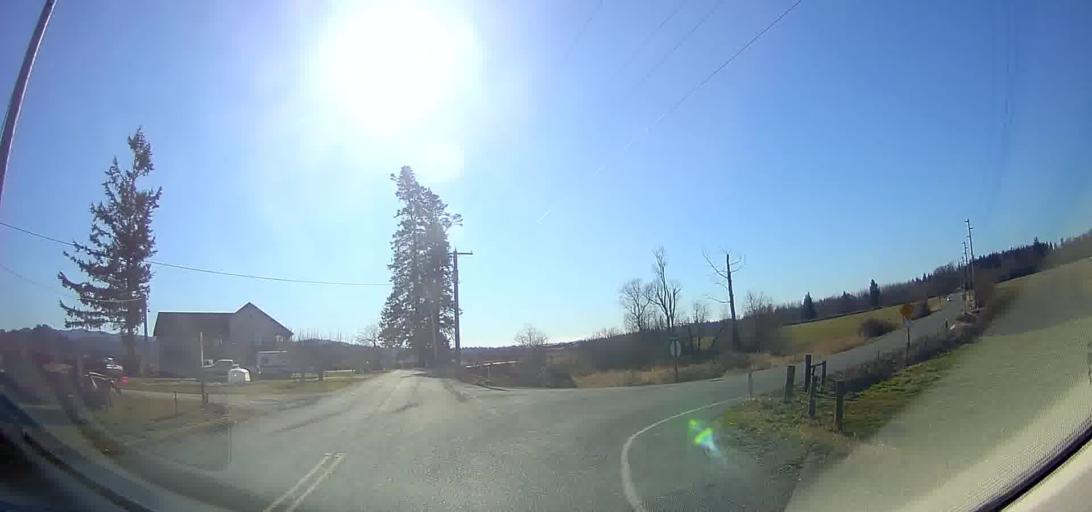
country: US
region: Washington
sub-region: Skagit County
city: Clear Lake
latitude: 48.4534
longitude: -122.2636
